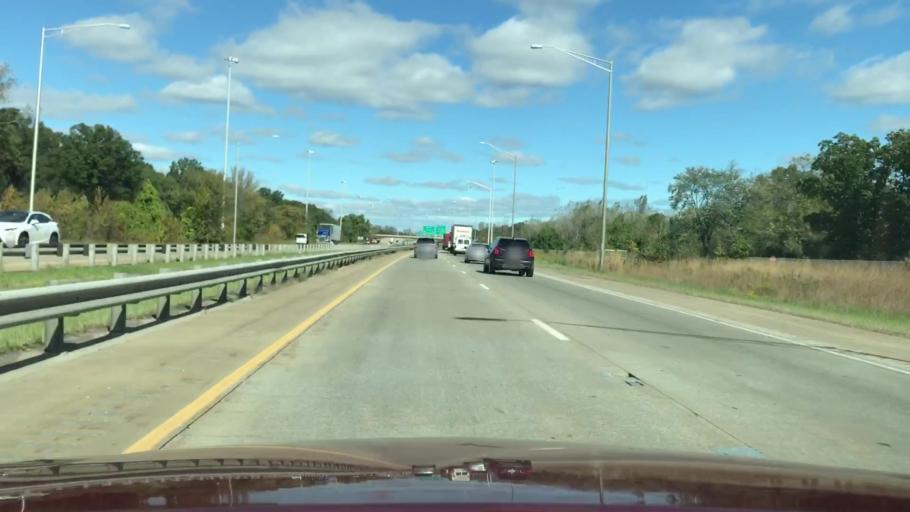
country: US
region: Illinois
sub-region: Cook County
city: Thornton
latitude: 41.5638
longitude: -87.5835
